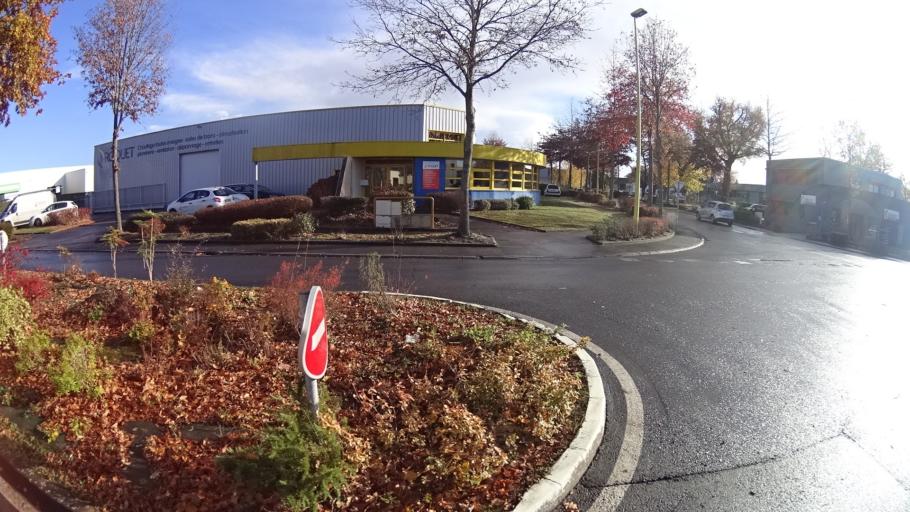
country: FR
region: Brittany
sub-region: Departement d'Ille-et-Vilaine
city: Redon
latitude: 47.6690
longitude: -2.0669
